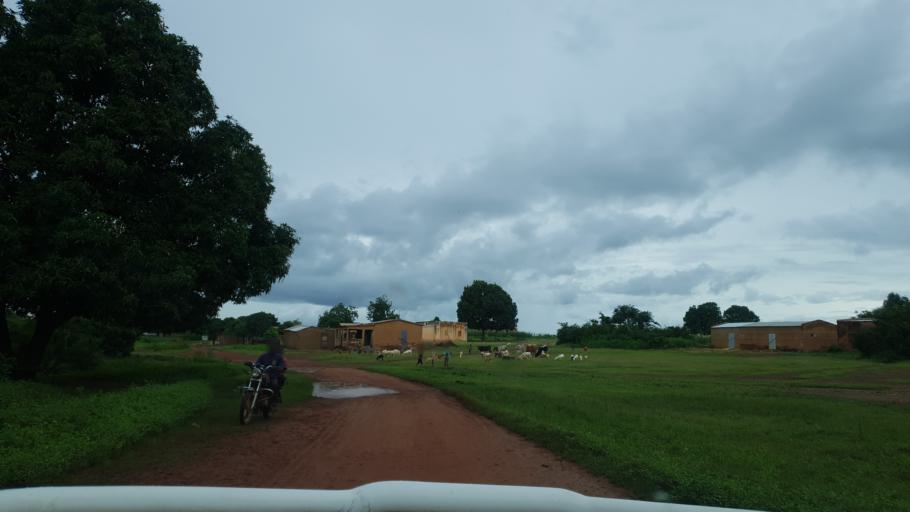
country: ML
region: Sikasso
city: Sikasso
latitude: 11.6743
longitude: -6.1700
